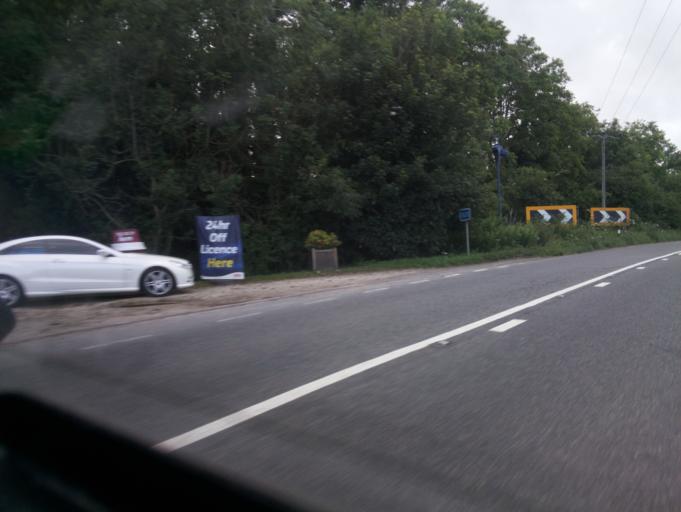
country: GB
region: England
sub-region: Gloucestershire
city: Shipton Village
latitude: 51.8705
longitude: -1.9638
